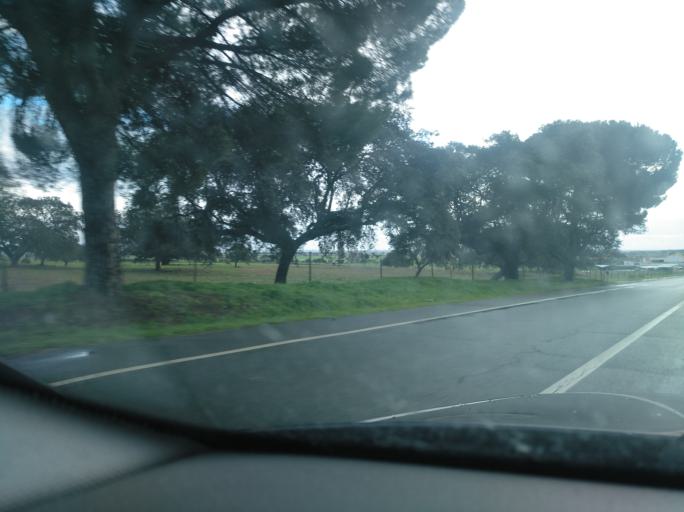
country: PT
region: Beja
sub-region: Aljustrel
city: Aljustrel
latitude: 37.9524
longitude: -8.3810
